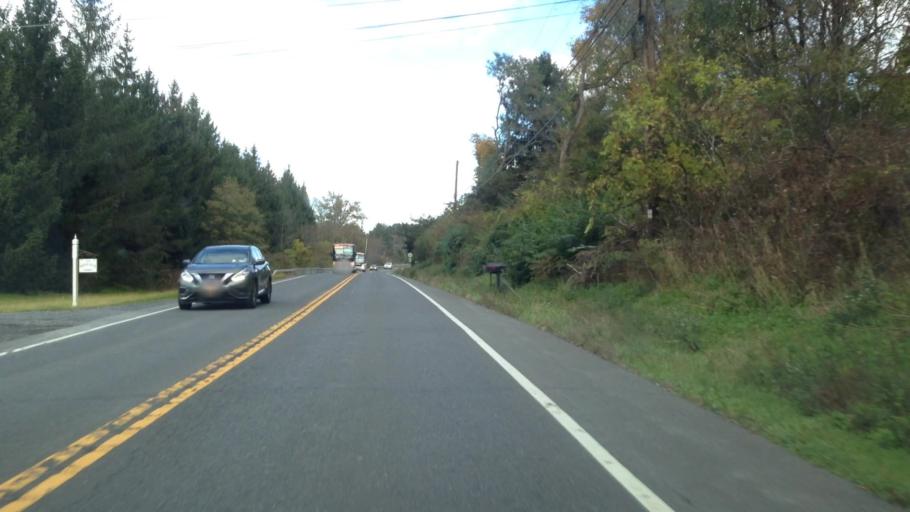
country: US
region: New York
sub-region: Ulster County
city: Tillson
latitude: 41.7985
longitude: -74.0661
